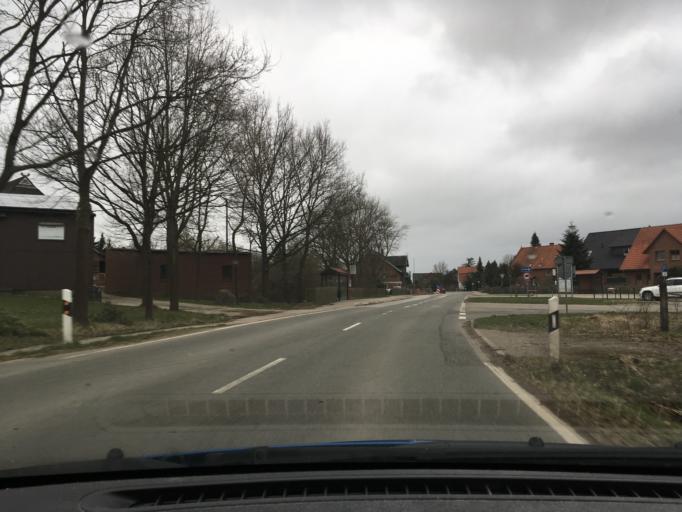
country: DE
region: Lower Saxony
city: Drage
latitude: 53.4061
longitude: 10.2598
